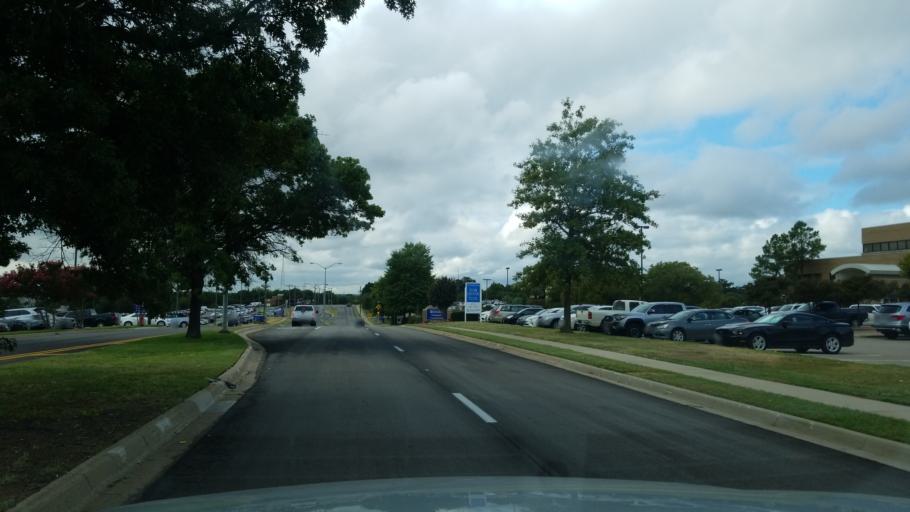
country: US
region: Texas
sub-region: Tarrant County
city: Bedford
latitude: 32.8361
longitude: -97.1254
